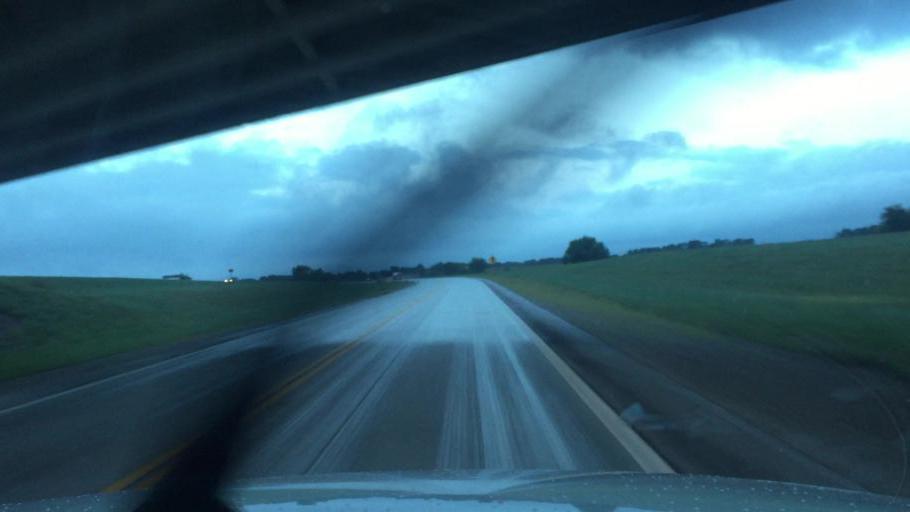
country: US
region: Kansas
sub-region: Neosho County
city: Chanute
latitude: 37.7258
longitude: -95.4710
